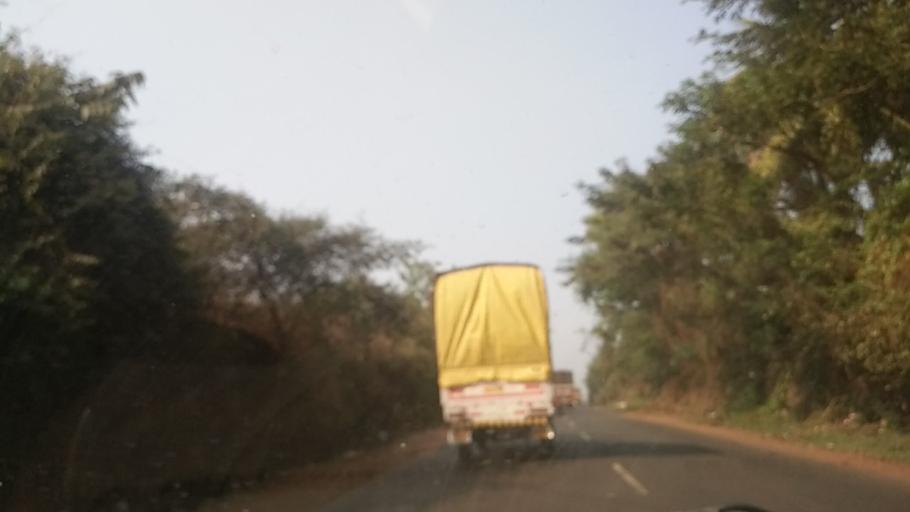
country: IN
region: Goa
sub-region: North Goa
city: Colovale
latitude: 15.6121
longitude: 73.8231
